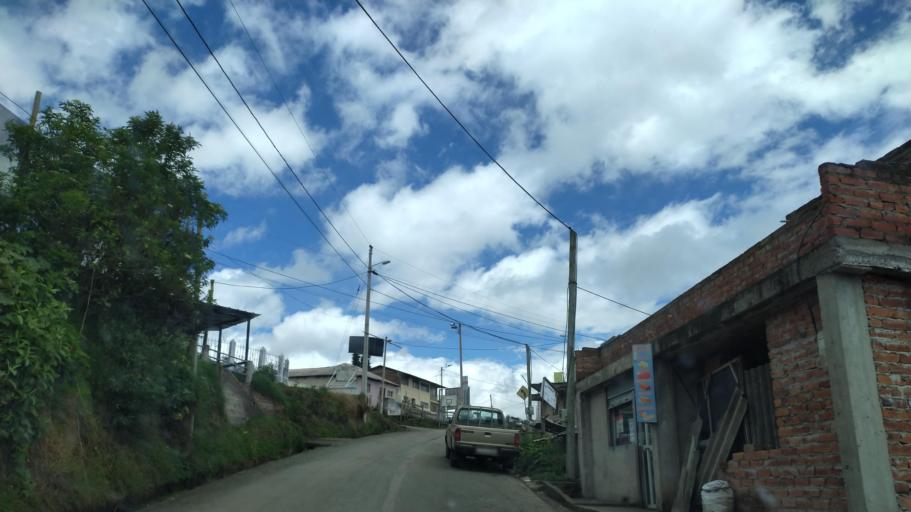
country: EC
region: Chimborazo
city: Riobamba
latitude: -1.6914
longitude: -78.5780
